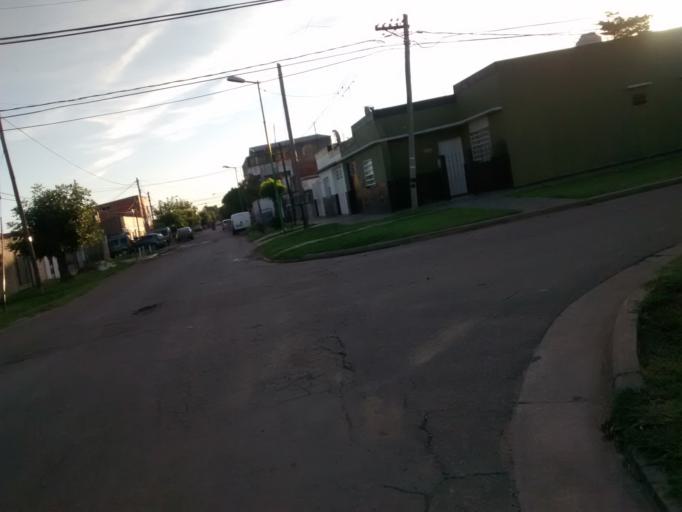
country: AR
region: Buenos Aires
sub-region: Partido de La Plata
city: La Plata
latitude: -34.9502
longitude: -57.9318
